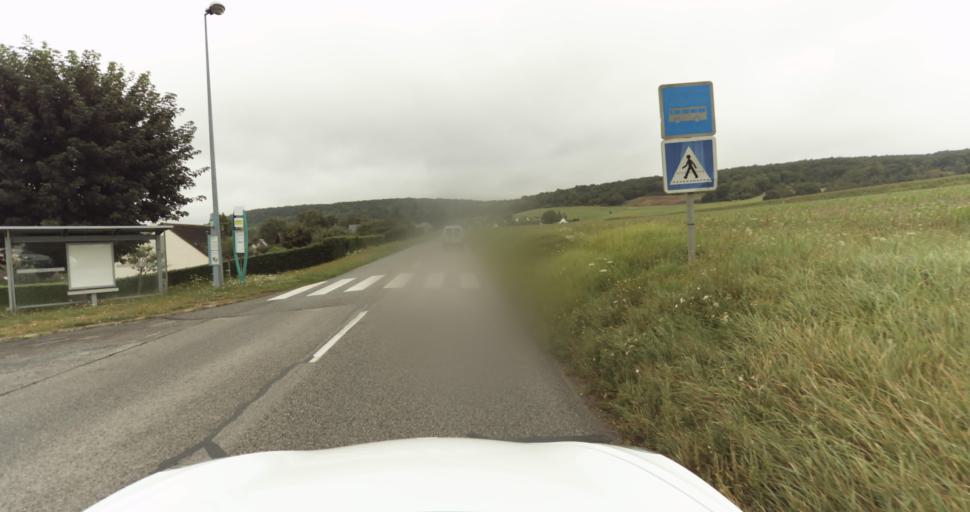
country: FR
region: Haute-Normandie
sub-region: Departement de l'Eure
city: Normanville
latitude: 49.0749
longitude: 1.1669
